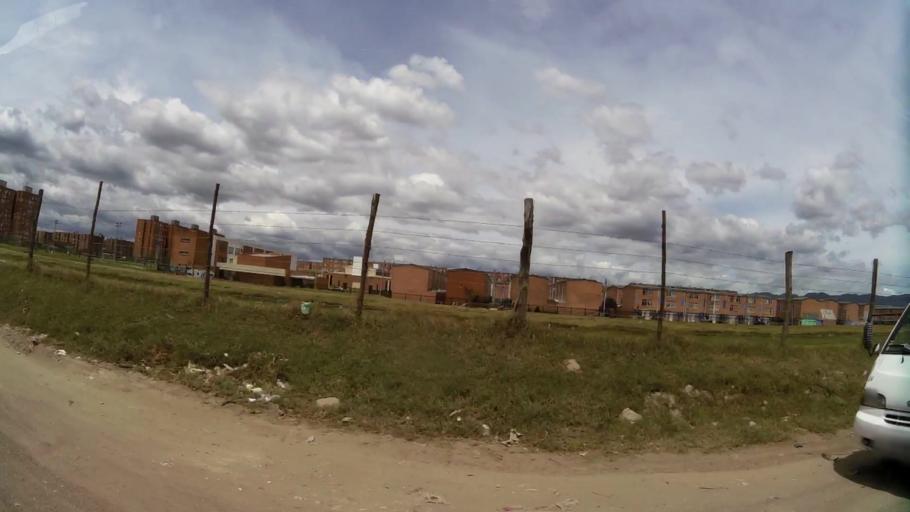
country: CO
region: Cundinamarca
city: Funza
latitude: 4.6479
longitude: -74.1629
